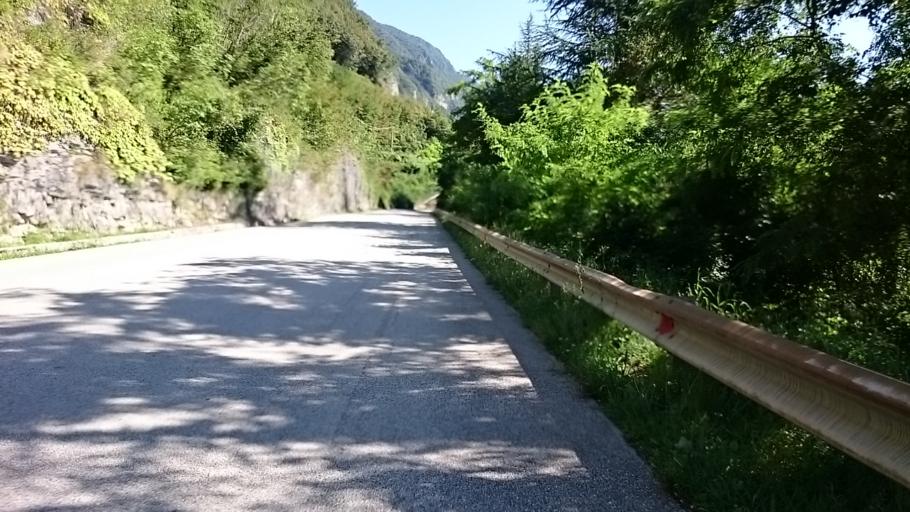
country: IT
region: Veneto
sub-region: Provincia di Belluno
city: Longarone
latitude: 46.2655
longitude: 12.3124
